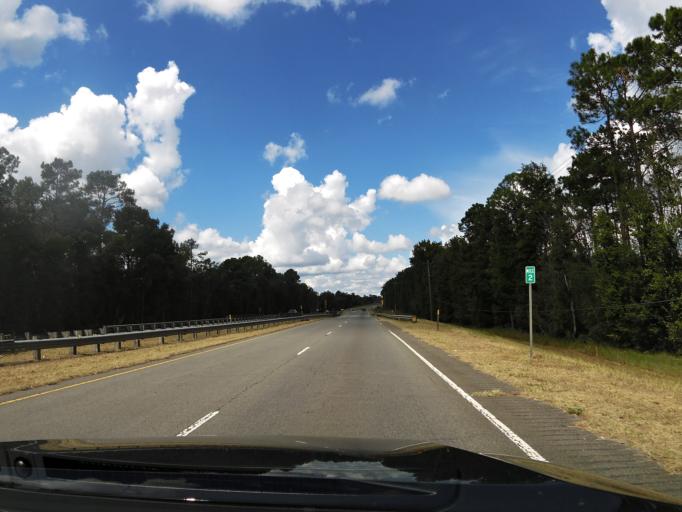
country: US
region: Georgia
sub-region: Charlton County
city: Folkston
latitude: 30.8027
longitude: -81.9910
